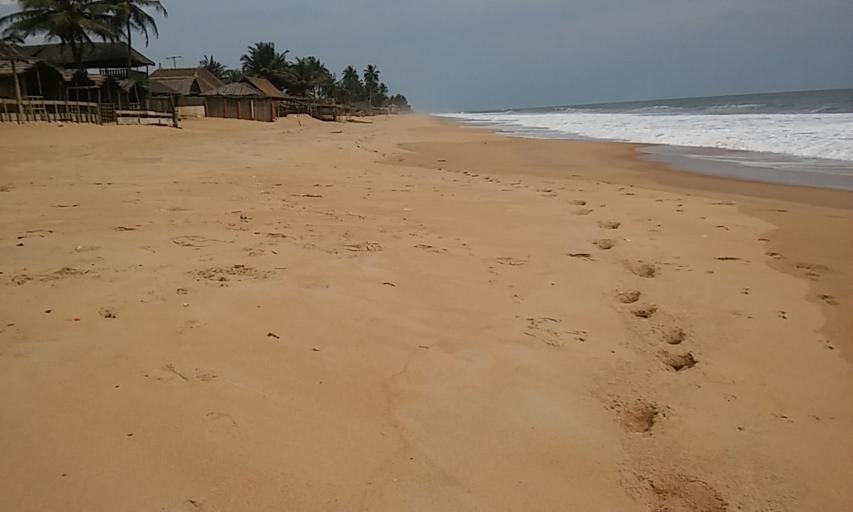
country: CI
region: Sud-Comoe
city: Grand-Bassam
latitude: 5.1975
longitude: -3.7548
